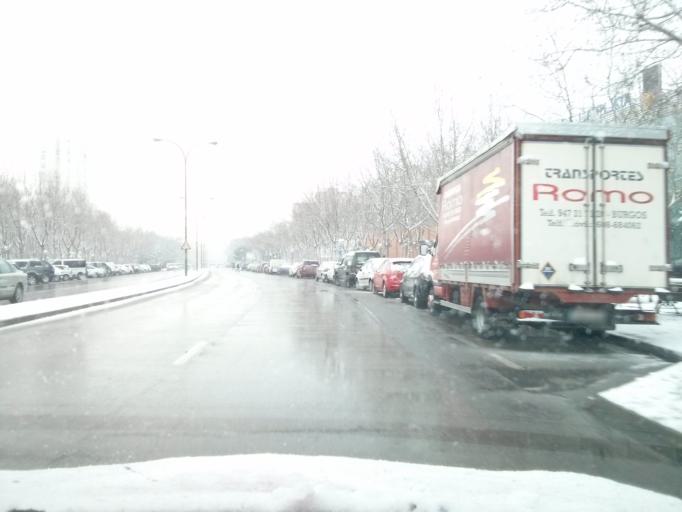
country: ES
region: Castille and Leon
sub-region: Provincia de Burgos
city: Burgos
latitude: 42.3486
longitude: -3.6831
